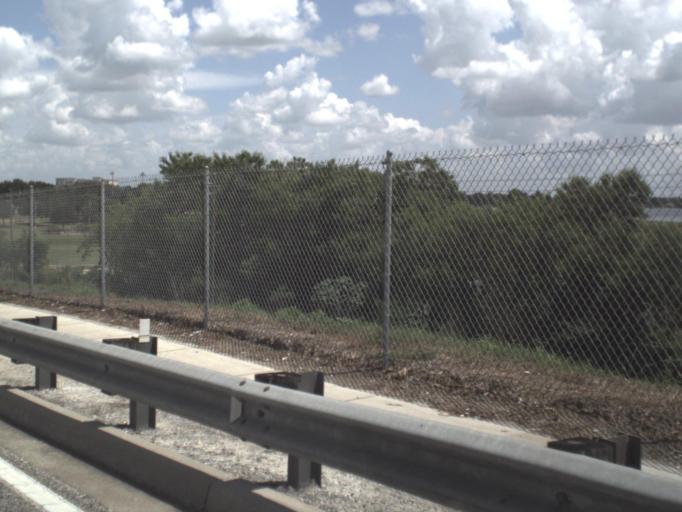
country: US
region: Florida
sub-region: Polk County
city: Winter Haven
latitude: 27.9984
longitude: -81.7343
